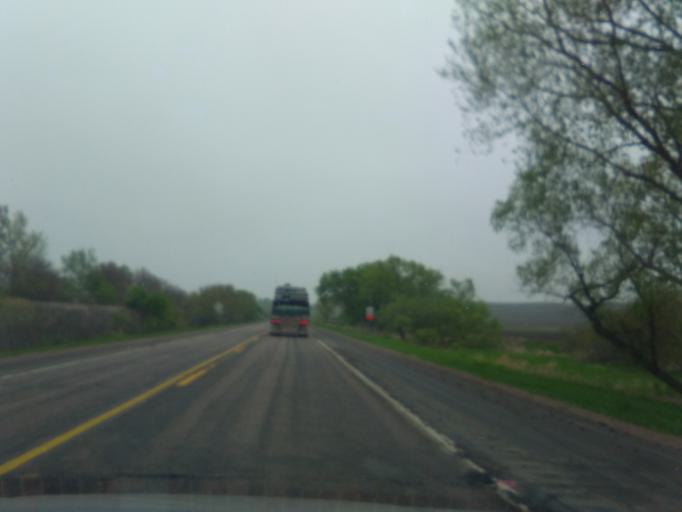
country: US
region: Nebraska
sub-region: Burt County
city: Oakland
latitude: 41.8113
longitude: -96.4757
